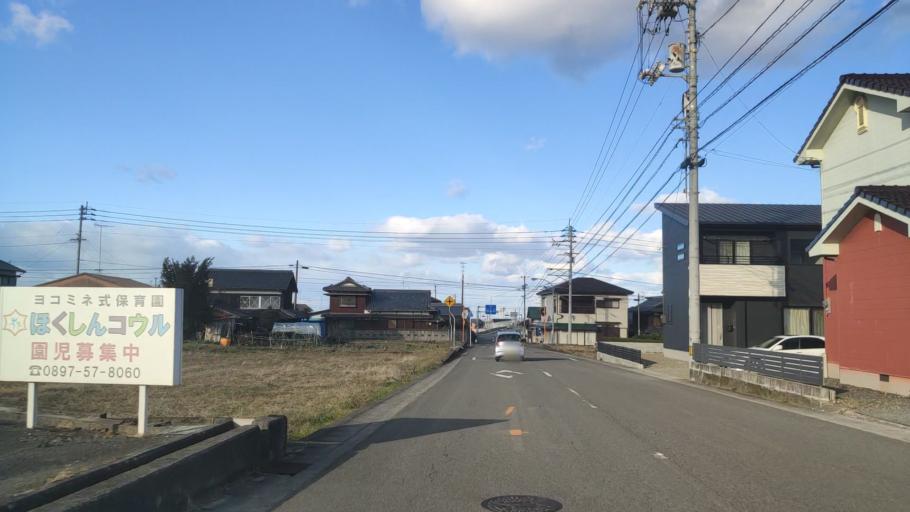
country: JP
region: Ehime
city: Saijo
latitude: 33.8937
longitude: 133.1322
